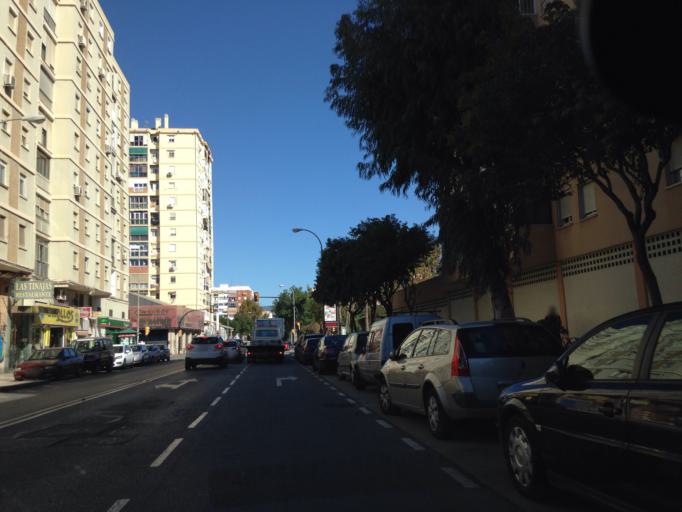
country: ES
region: Andalusia
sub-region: Provincia de Malaga
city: Malaga
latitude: 36.6911
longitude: -4.4503
